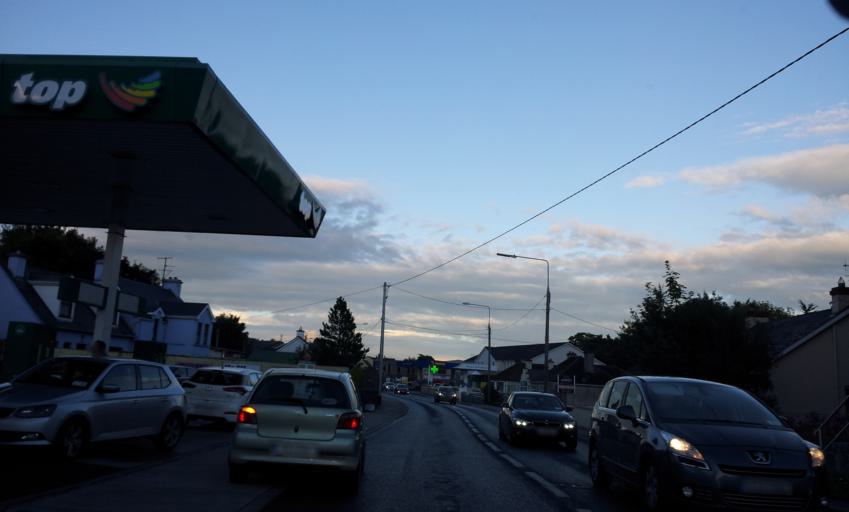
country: IE
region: Munster
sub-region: County Limerick
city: Newcastle West
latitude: 52.4487
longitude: -9.0558
